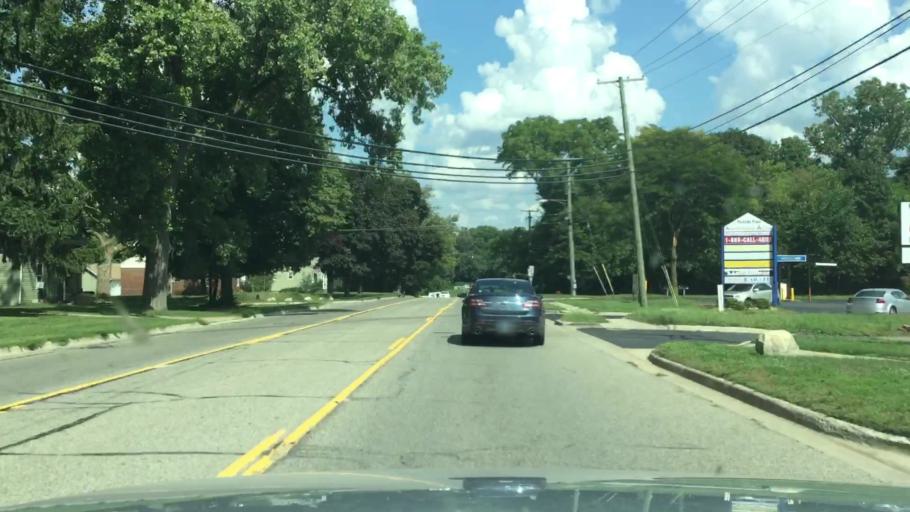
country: US
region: Michigan
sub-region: Washtenaw County
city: Saline
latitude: 42.1619
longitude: -83.7933
